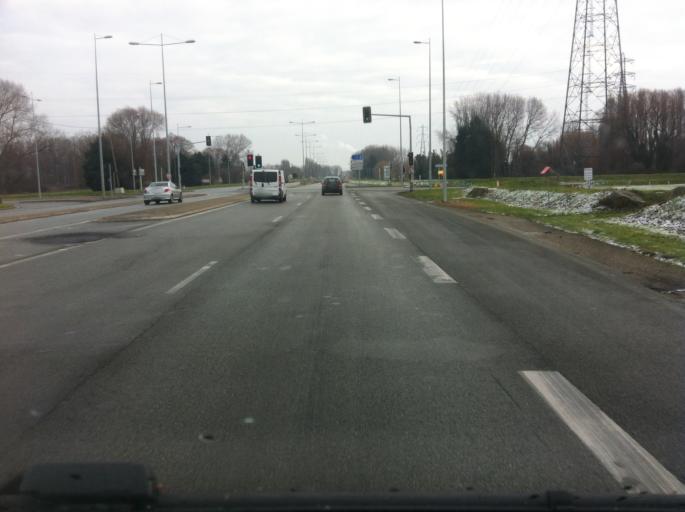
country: FR
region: Haute-Normandie
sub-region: Departement de la Seine-Maritime
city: Harfleur
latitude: 49.4877
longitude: 0.1951
